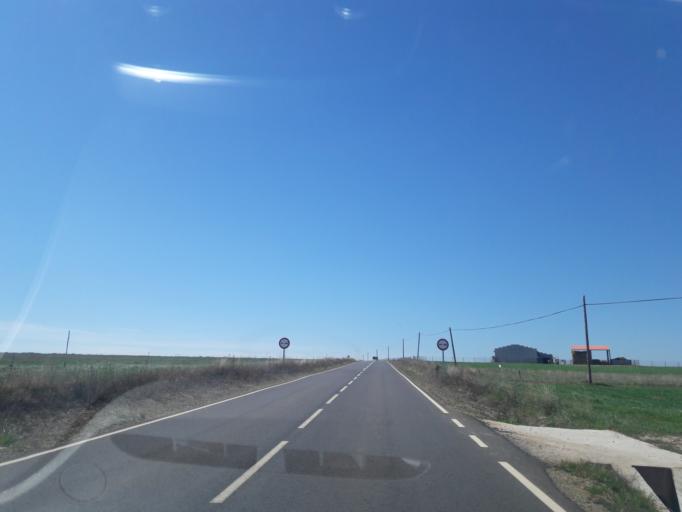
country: ES
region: Castille and Leon
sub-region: Provincia de Salamanca
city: Martinamor
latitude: 40.8135
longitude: -5.5929
